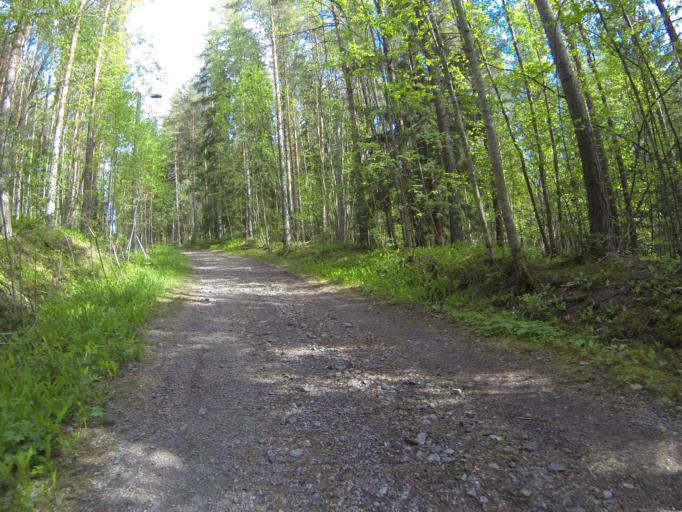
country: FI
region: Varsinais-Suomi
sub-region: Salo
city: Salo
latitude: 60.3864
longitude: 23.1731
